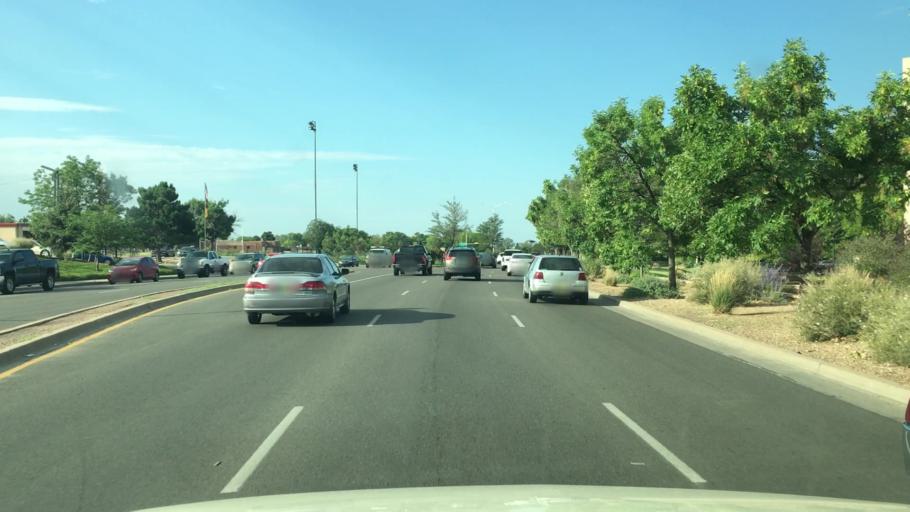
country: US
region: New Mexico
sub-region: Santa Fe County
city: Santa Fe
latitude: 35.6736
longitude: -105.9540
